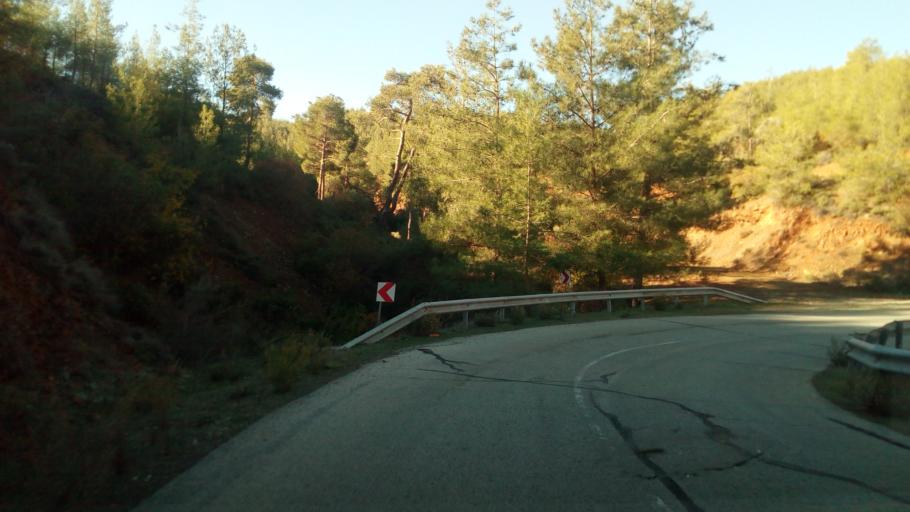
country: CY
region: Lefkosia
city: Lefka
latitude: 35.0667
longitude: 32.8151
